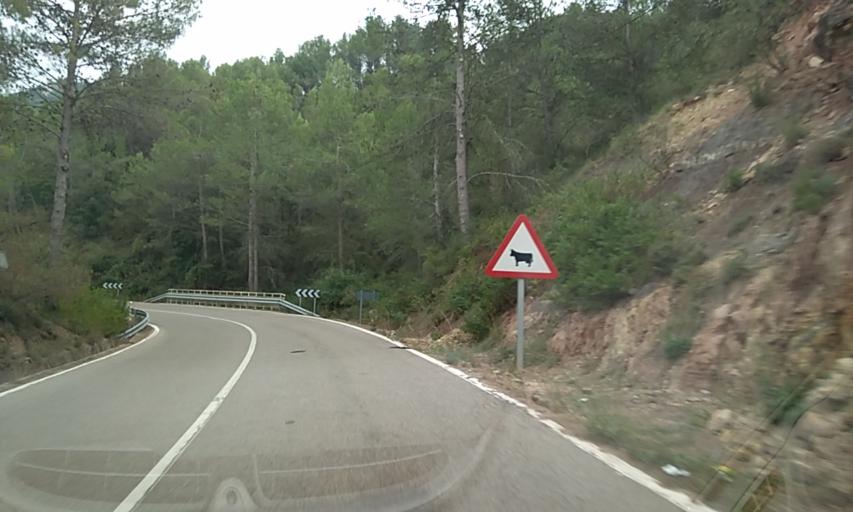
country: ES
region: Valencia
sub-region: Provincia de Castello
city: Puebla de Arenoso
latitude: 40.0882
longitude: -0.5679
